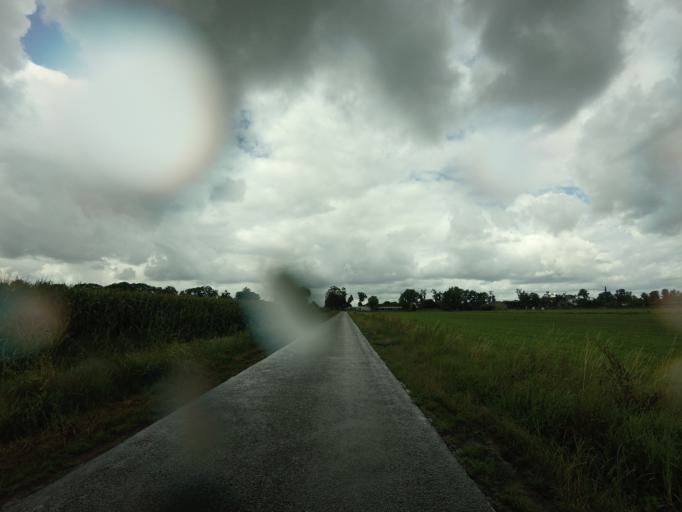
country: NL
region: Overijssel
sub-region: Gemeente Steenwijkerland
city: Wanneperveen
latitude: 52.7209
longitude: 6.1560
